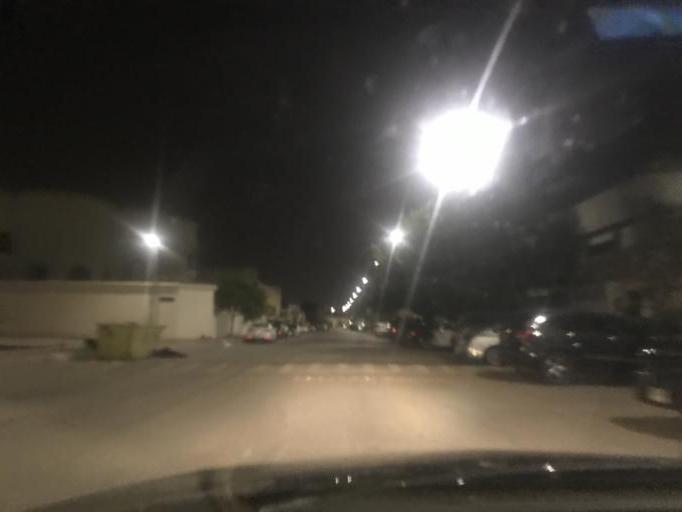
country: SA
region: Ar Riyad
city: Riyadh
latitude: 24.7365
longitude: 46.7686
